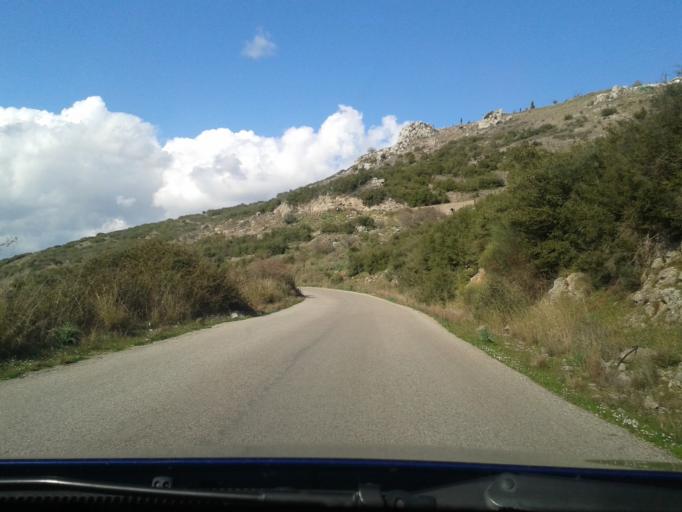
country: GR
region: West Greece
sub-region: Nomos Aitolias kai Akarnanias
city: Fitiai
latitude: 38.6910
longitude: 21.1785
